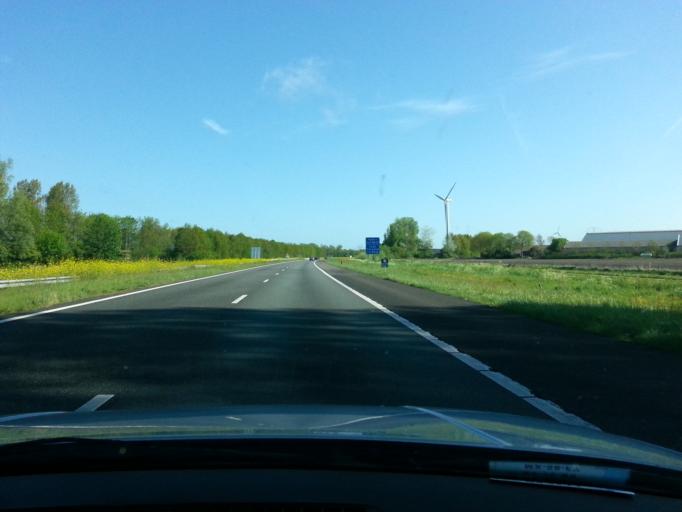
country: NL
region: Flevoland
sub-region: Gemeente Lelystad
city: Lelystad
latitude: 52.5591
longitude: 5.5309
